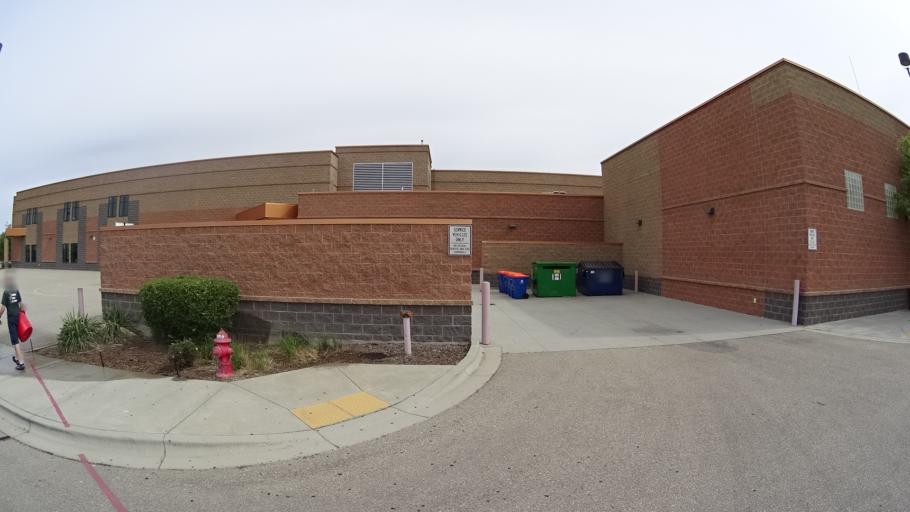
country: US
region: Idaho
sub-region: Ada County
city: Garden City
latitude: 43.5704
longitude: -116.2858
